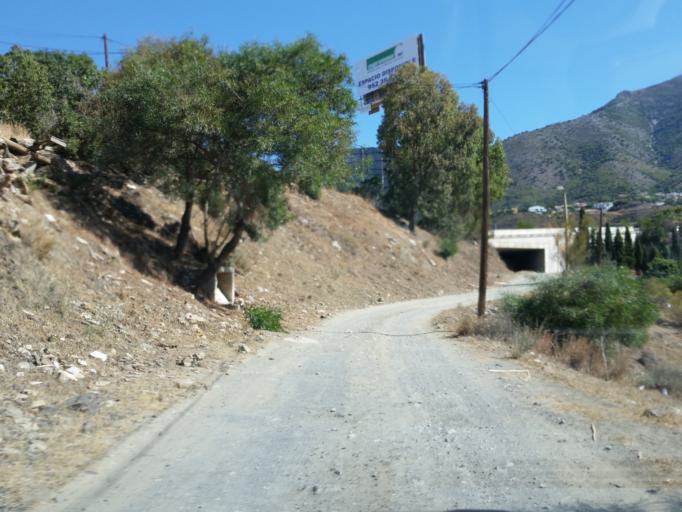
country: ES
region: Andalusia
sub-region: Provincia de Malaga
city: Mijas
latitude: 36.5789
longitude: -4.6084
